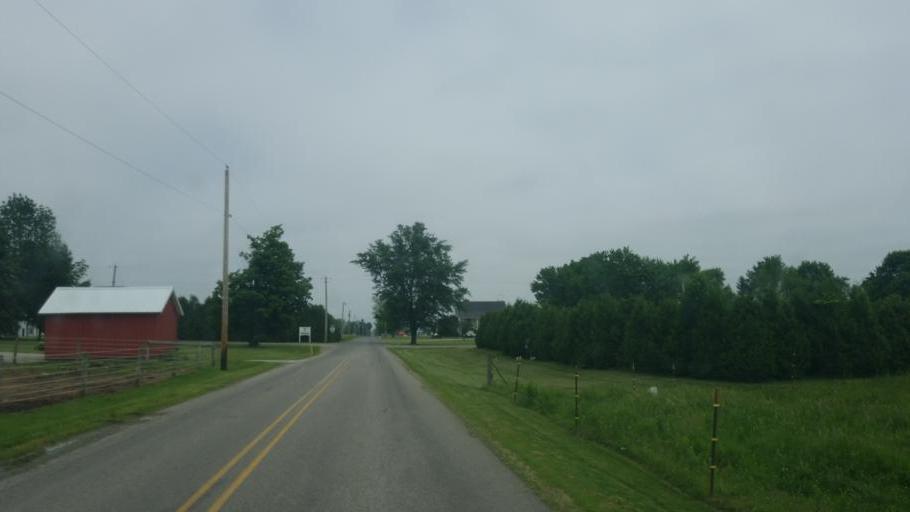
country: US
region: Indiana
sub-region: Elkhart County
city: Nappanee
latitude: 41.4709
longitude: -86.0208
